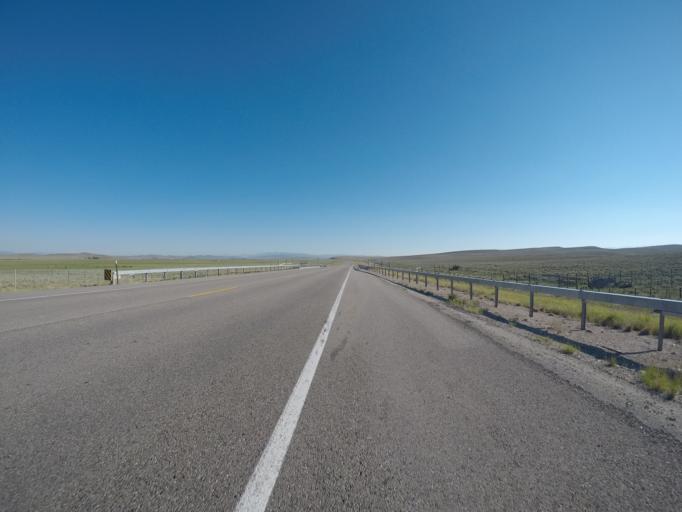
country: US
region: Wyoming
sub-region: Sublette County
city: Pinedale
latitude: 42.9247
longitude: -110.0808
